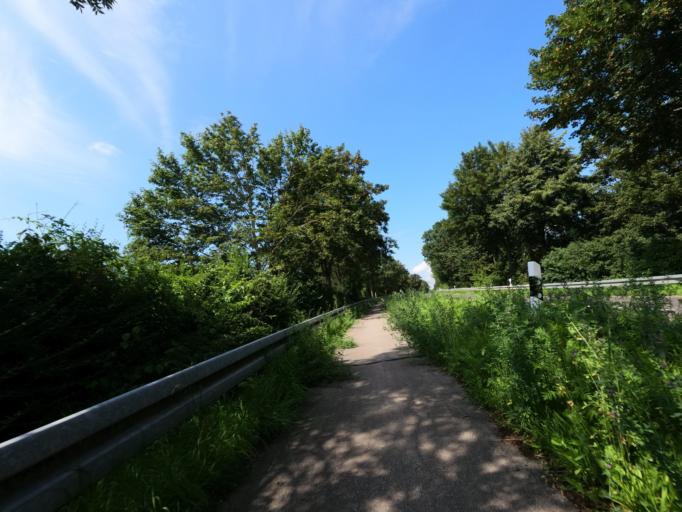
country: DE
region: North Rhine-Westphalia
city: Geilenkirchen
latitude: 50.9517
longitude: 6.1386
